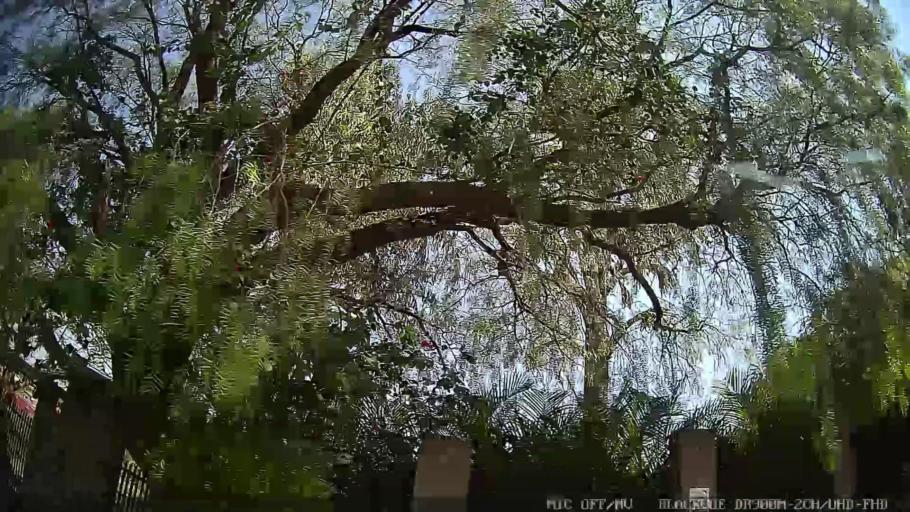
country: BR
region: Sao Paulo
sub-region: Vinhedo
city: Vinhedo
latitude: -23.0407
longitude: -46.9825
